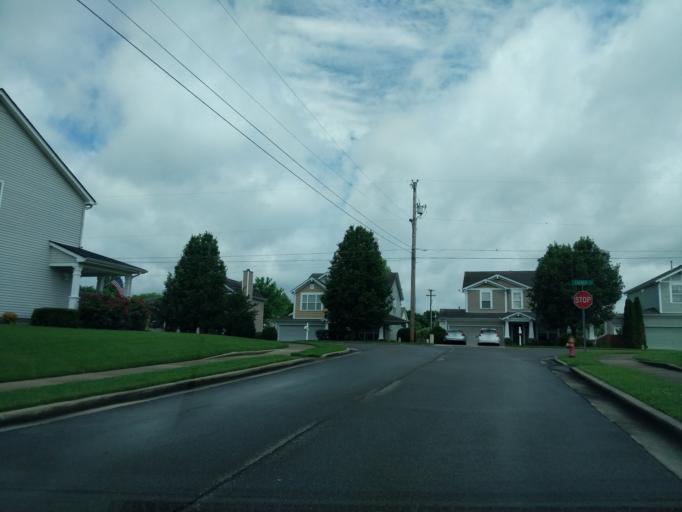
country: US
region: Tennessee
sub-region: Davidson County
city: Lakewood
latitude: 36.2337
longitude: -86.6930
